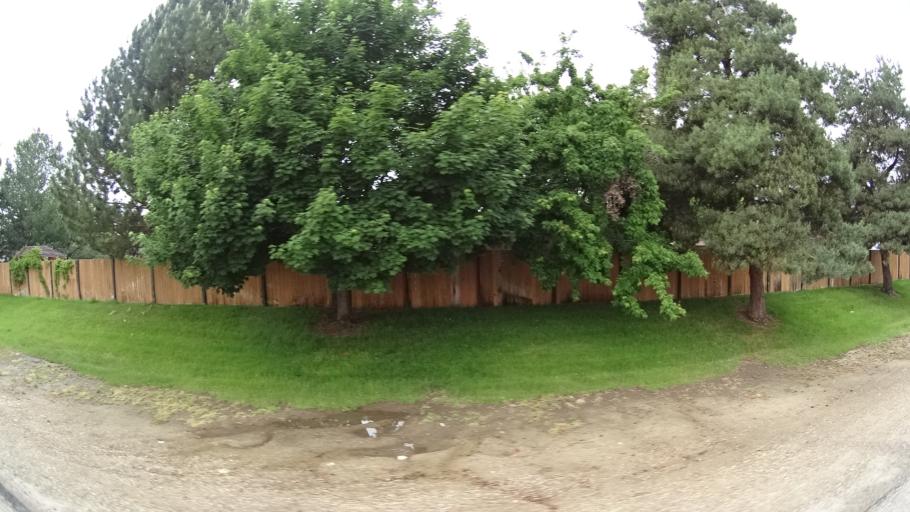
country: US
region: Idaho
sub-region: Ada County
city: Eagle
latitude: 43.7089
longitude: -116.3144
